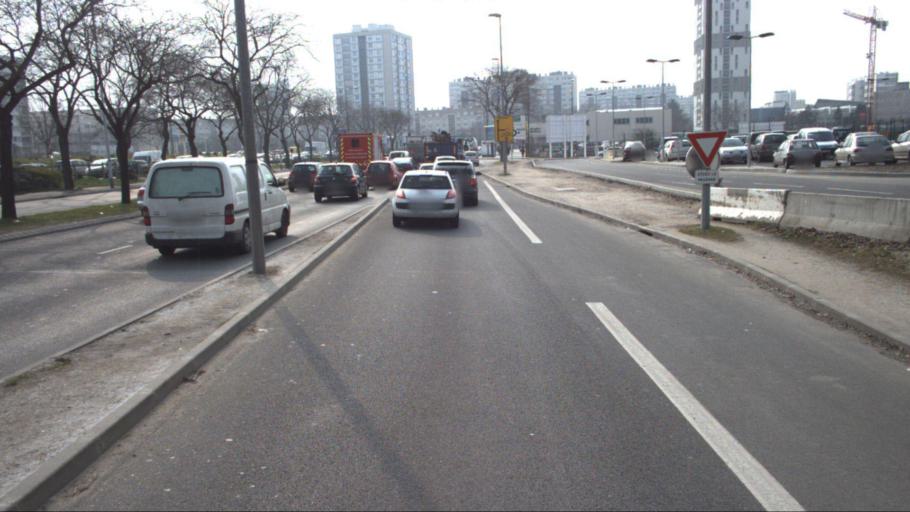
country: FR
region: Ile-de-France
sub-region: Departement des Hauts-de-Seine
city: Bois-Colombes
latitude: 48.9324
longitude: 2.2826
